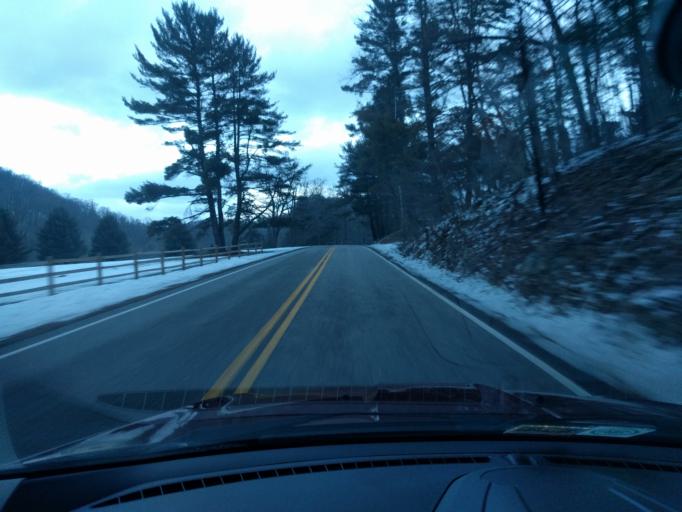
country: US
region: Virginia
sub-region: Bath County
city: Warm Springs
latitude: 37.9494
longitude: -79.8700
